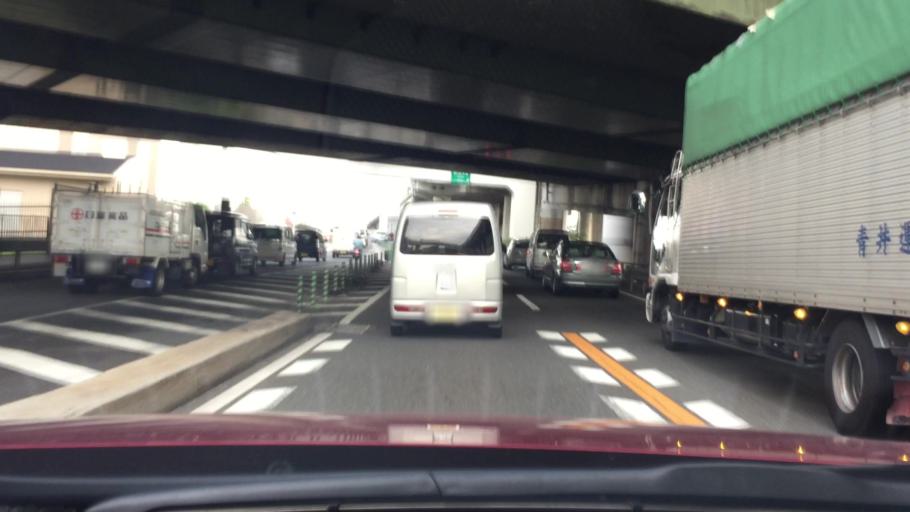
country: JP
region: Osaka
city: Kadoma
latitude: 34.7545
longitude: 135.5757
